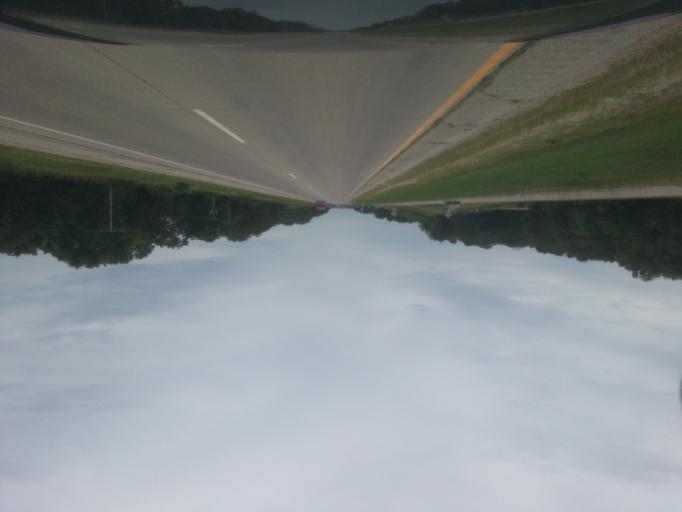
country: US
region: Wisconsin
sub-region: Dane County
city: McFarland
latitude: 43.0432
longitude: -89.2584
